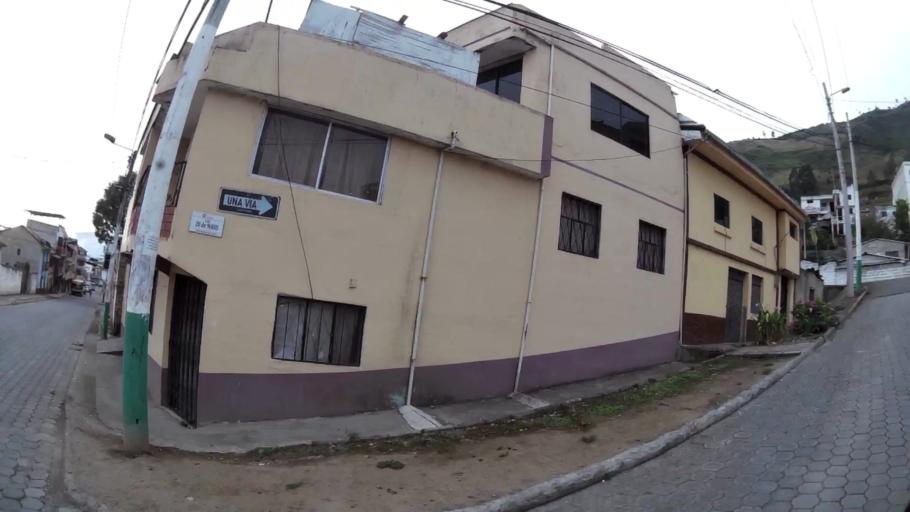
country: EC
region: Chimborazo
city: Alausi
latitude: -2.2909
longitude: -78.9163
